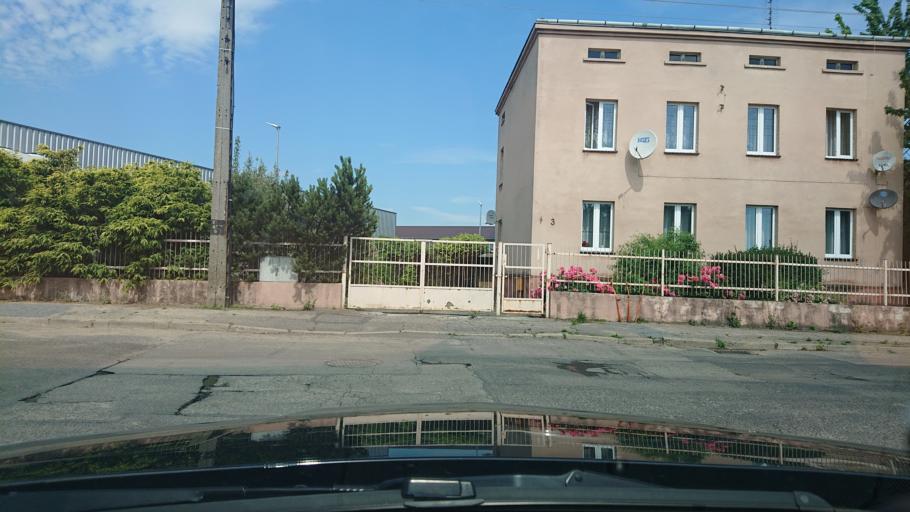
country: PL
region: Greater Poland Voivodeship
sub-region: Powiat gnieznienski
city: Gniezno
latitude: 52.5249
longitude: 17.6023
